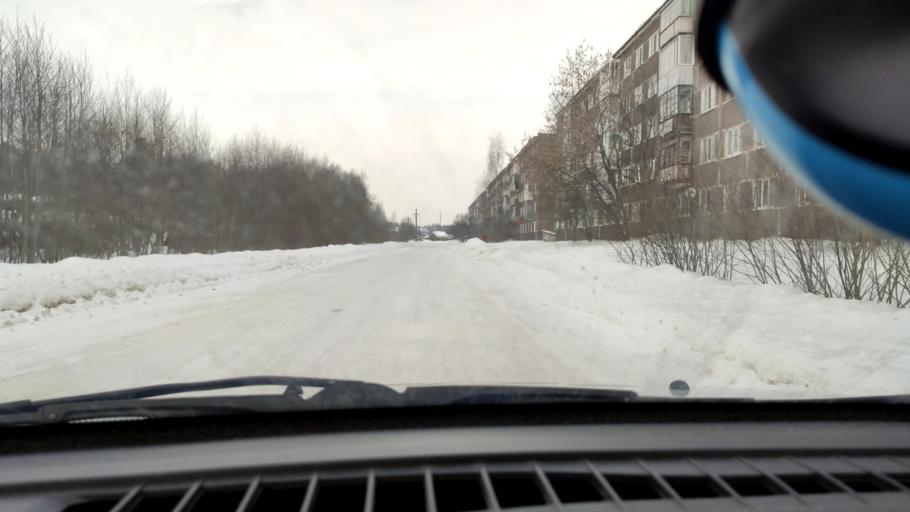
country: RU
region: Perm
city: Overyata
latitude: 58.0768
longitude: 55.8703
